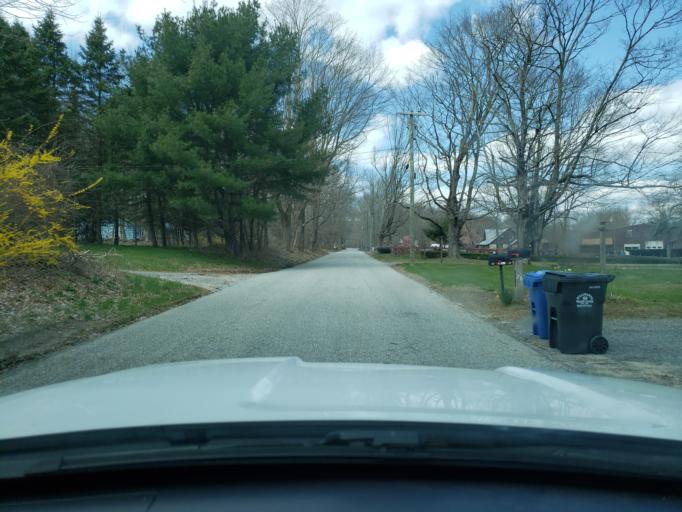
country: US
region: Connecticut
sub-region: Windham County
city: Plainfield Village
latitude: 41.6997
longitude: -71.9658
